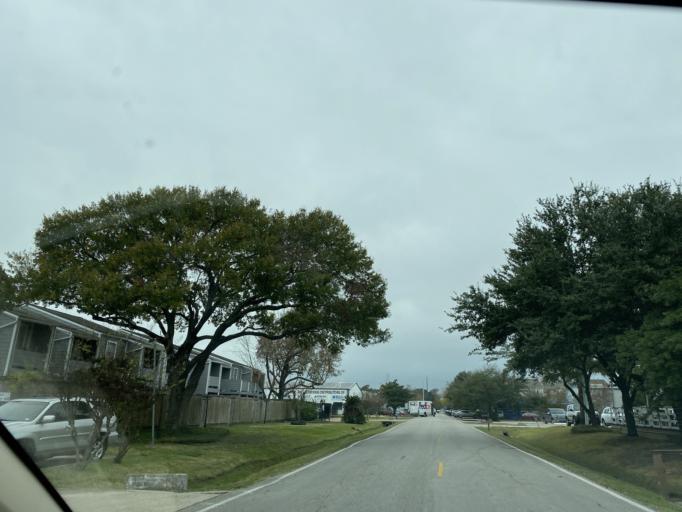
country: US
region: Texas
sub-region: Harris County
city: Bellaire
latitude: 29.7302
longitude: -95.4805
